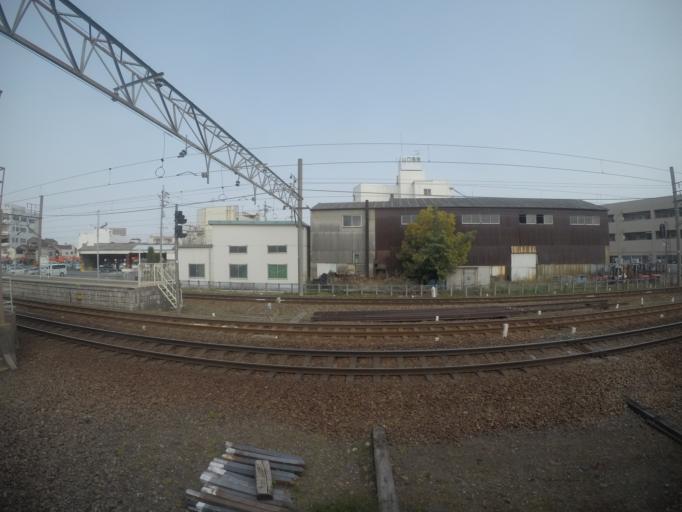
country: JP
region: Aichi
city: Nagoya-shi
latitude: 35.0919
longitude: 136.9126
